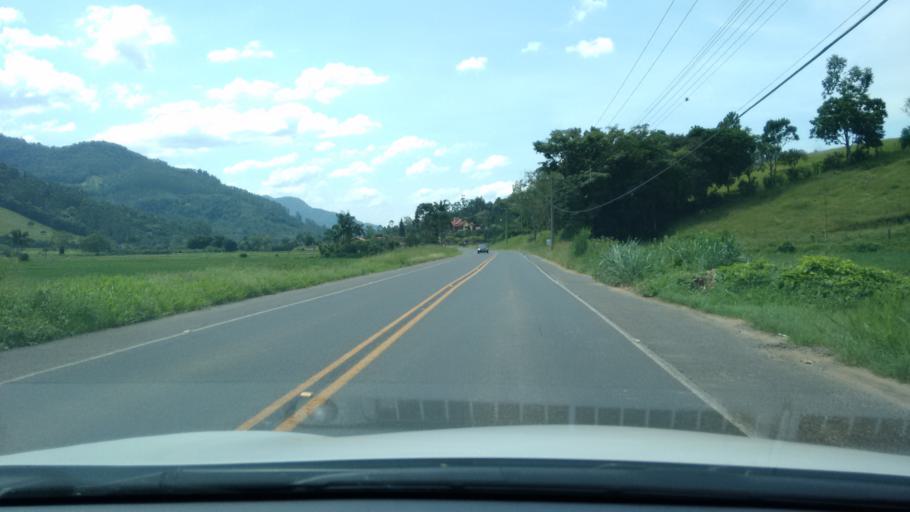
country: BR
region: Santa Catarina
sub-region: Rodeio
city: Gavea
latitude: -26.8781
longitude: -49.3424
